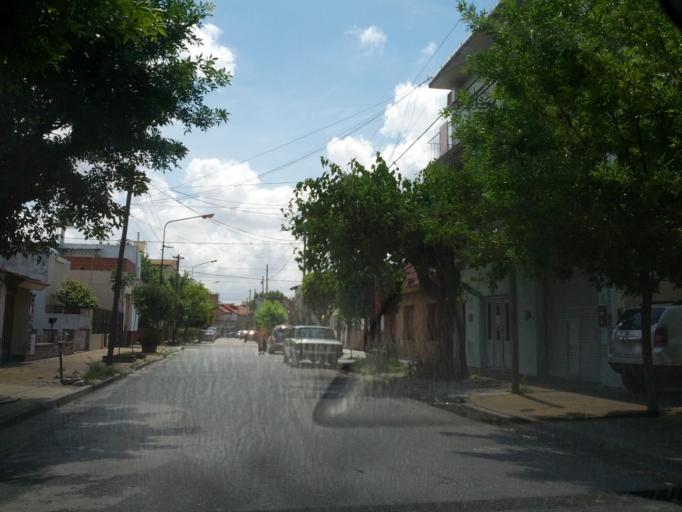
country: AR
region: Buenos Aires
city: San Justo
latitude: -34.6446
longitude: -58.5455
